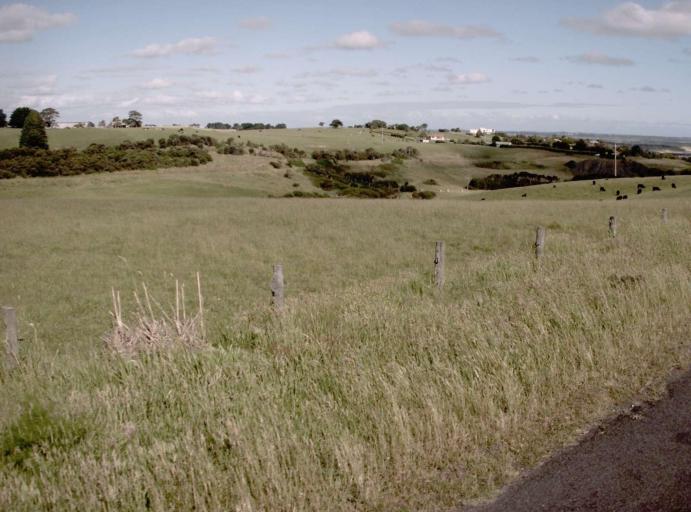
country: AU
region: Victoria
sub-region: Bass Coast
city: North Wonthaggi
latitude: -38.5399
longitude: 145.4584
